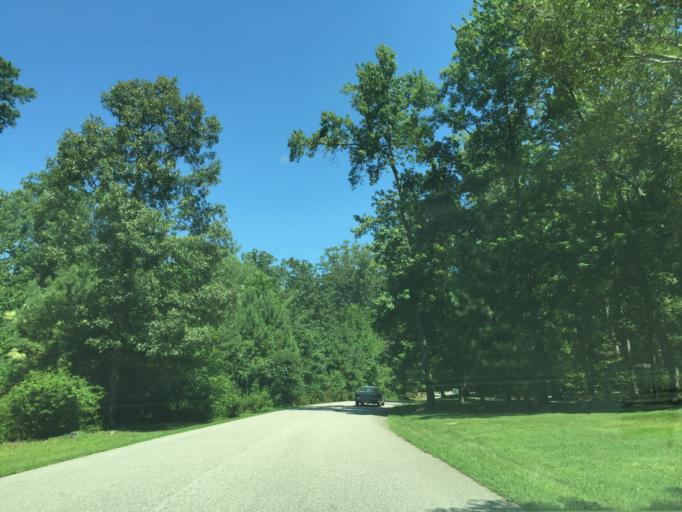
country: US
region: Virginia
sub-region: City of Newport News
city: Newport News
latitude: 37.0514
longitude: -76.4894
